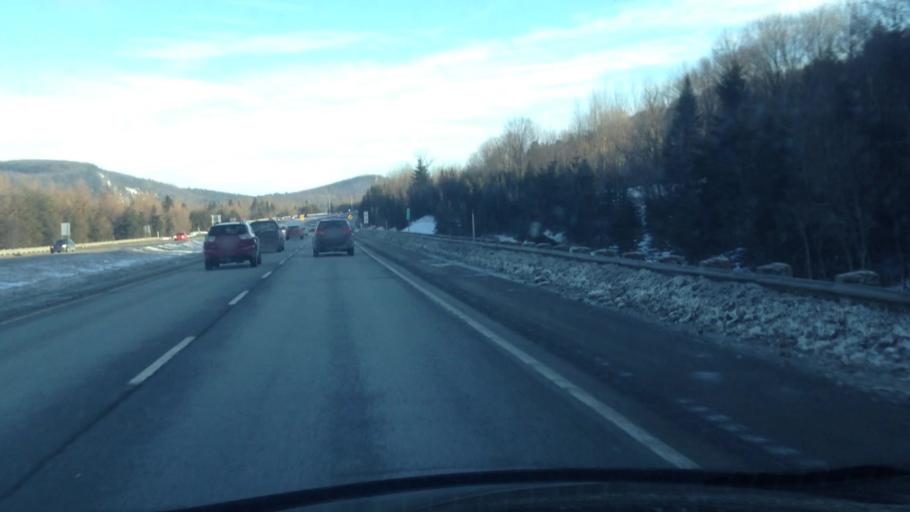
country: CA
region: Quebec
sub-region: Laurentides
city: Prevost
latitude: 45.8856
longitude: -74.1164
